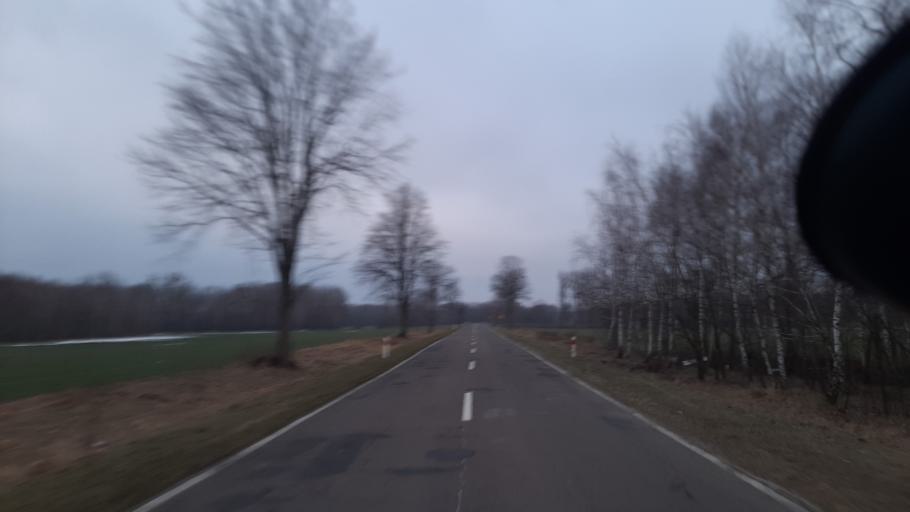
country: PL
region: Lublin Voivodeship
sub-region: Powiat parczewski
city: Sosnowica
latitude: 51.5967
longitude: 23.1552
